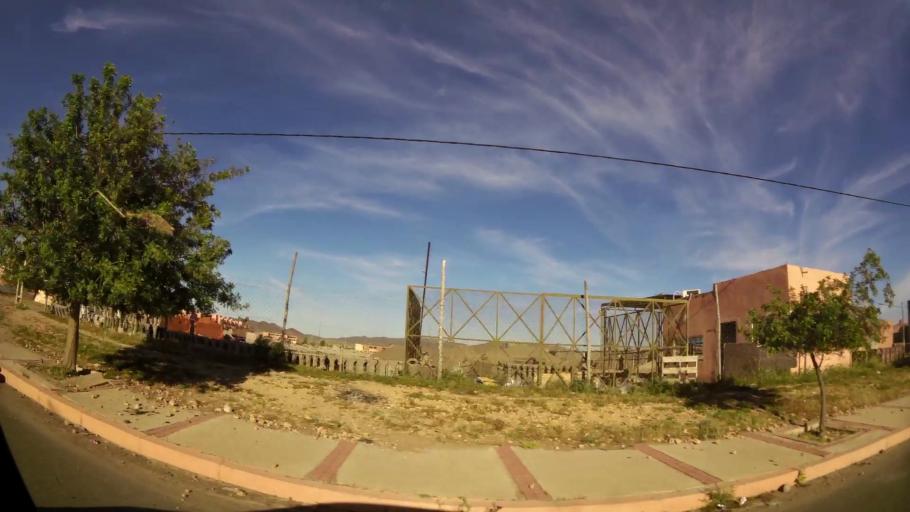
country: MA
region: Marrakech-Tensift-Al Haouz
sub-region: Marrakech
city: Marrakesh
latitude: 31.7528
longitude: -8.1002
